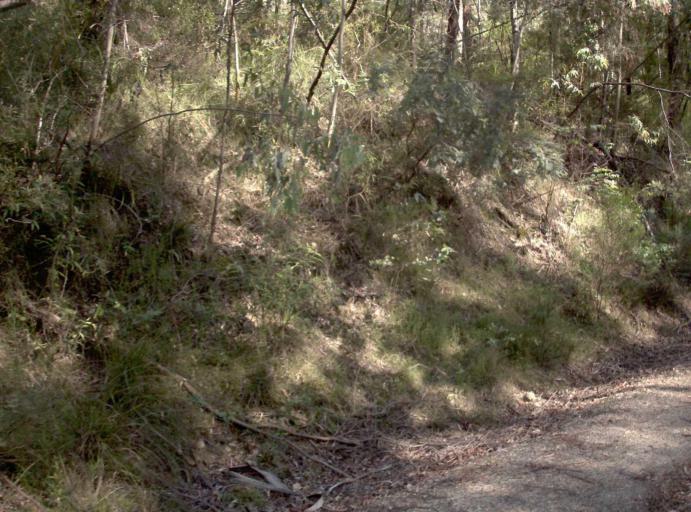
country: AU
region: Victoria
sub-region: East Gippsland
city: Lakes Entrance
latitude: -37.4871
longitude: 148.5530
